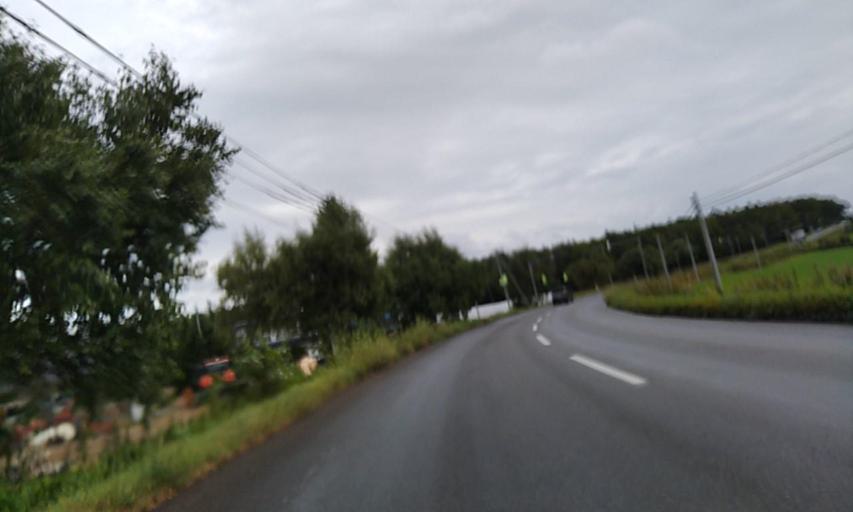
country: JP
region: Hokkaido
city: Kitami
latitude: 44.1025
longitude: 143.9673
